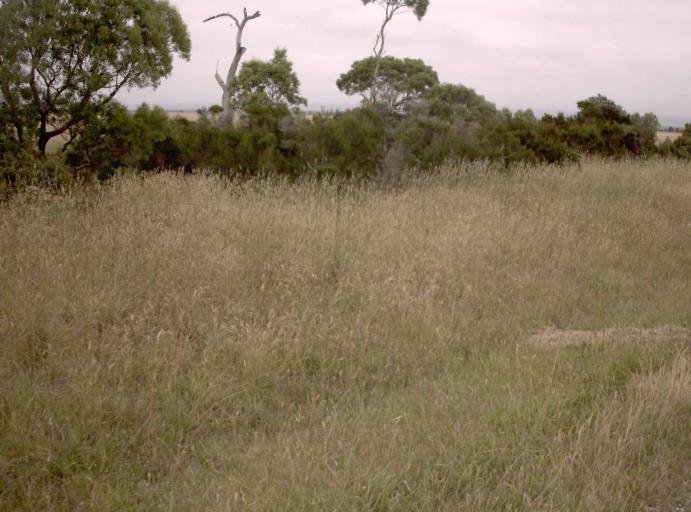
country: AU
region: Victoria
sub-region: Wellington
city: Heyfield
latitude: -38.1220
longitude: 146.7808
